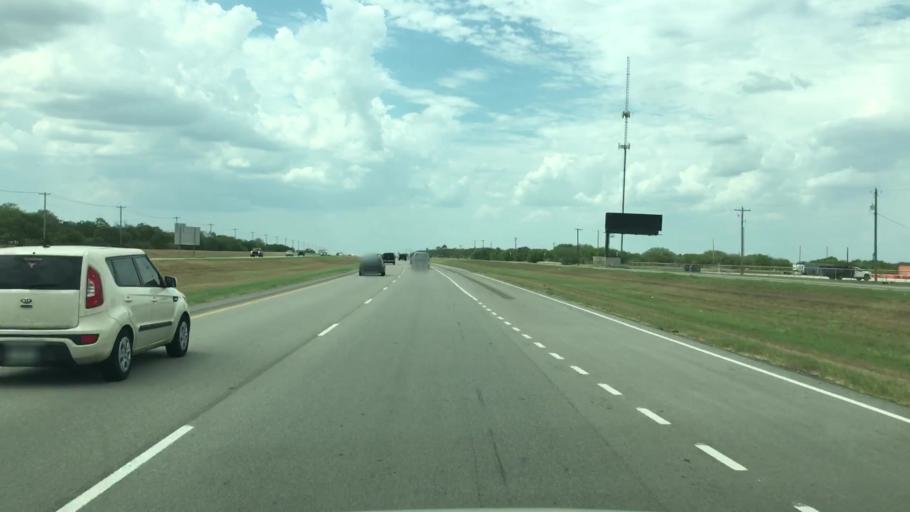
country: US
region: Texas
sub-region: Live Oak County
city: Three Rivers
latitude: 28.4940
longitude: -98.1478
